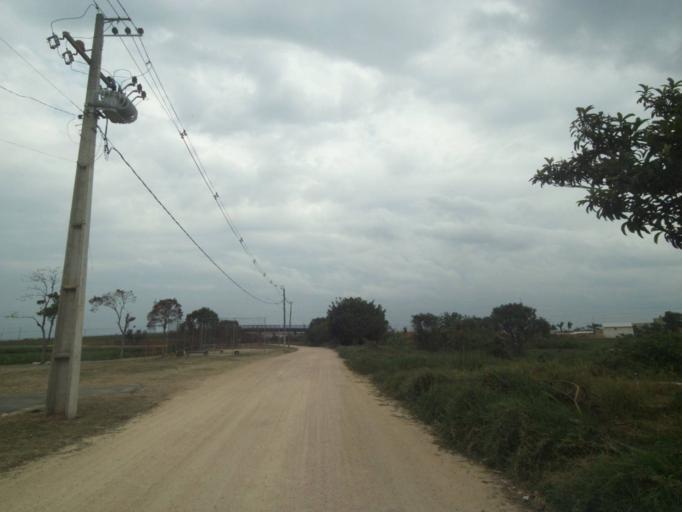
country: BR
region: Parana
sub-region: Sao Jose Dos Pinhais
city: Sao Jose dos Pinhais
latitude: -25.4997
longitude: -49.2060
